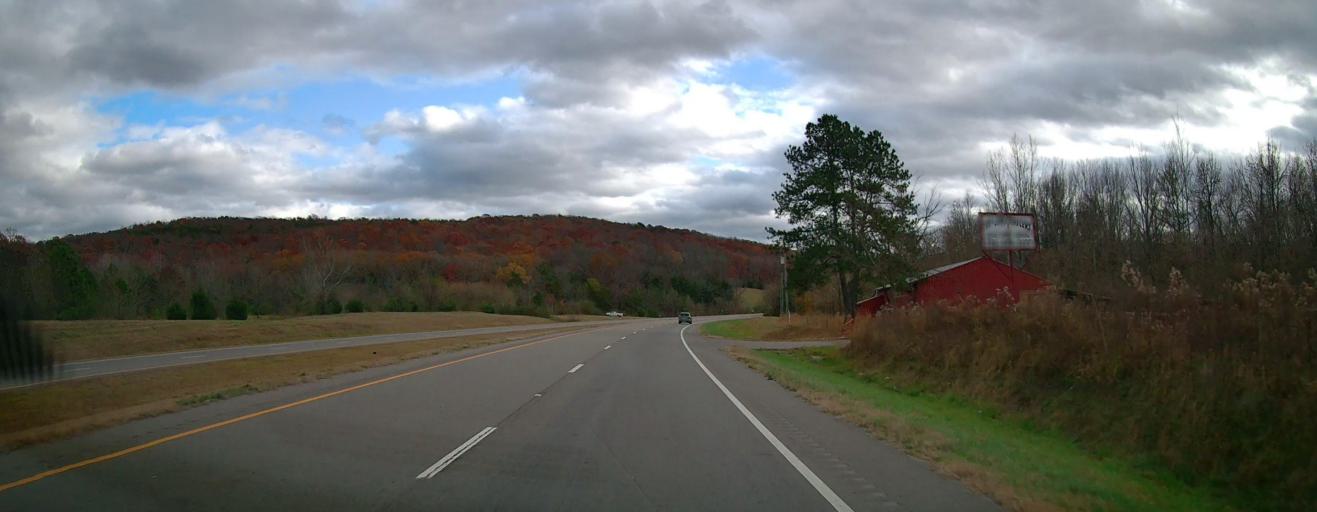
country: US
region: Alabama
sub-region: Morgan County
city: Falkville
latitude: 34.3271
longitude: -87.0035
